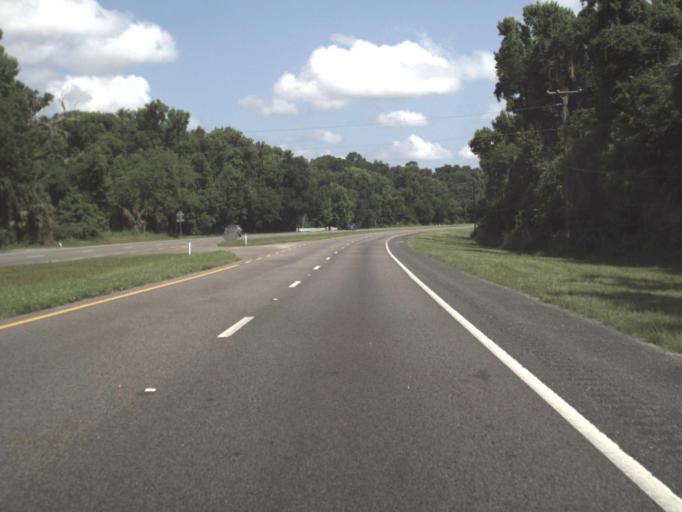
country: US
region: Florida
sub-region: Alachua County
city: Gainesville
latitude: 29.5232
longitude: -82.3040
